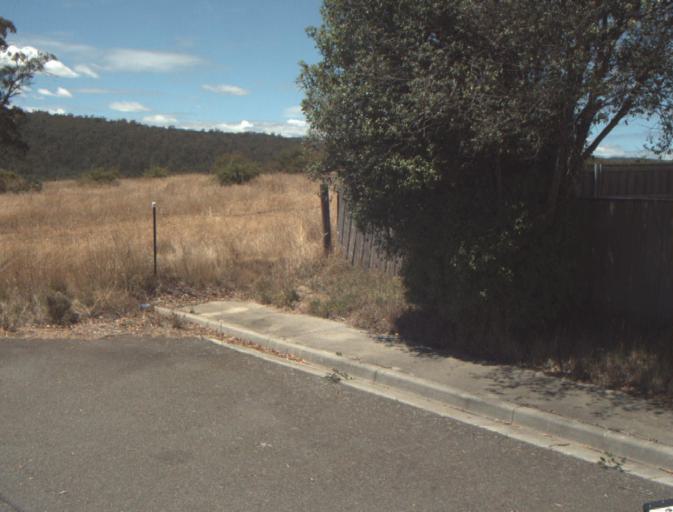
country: AU
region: Tasmania
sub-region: Launceston
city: Mayfield
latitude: -41.3736
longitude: 147.1381
